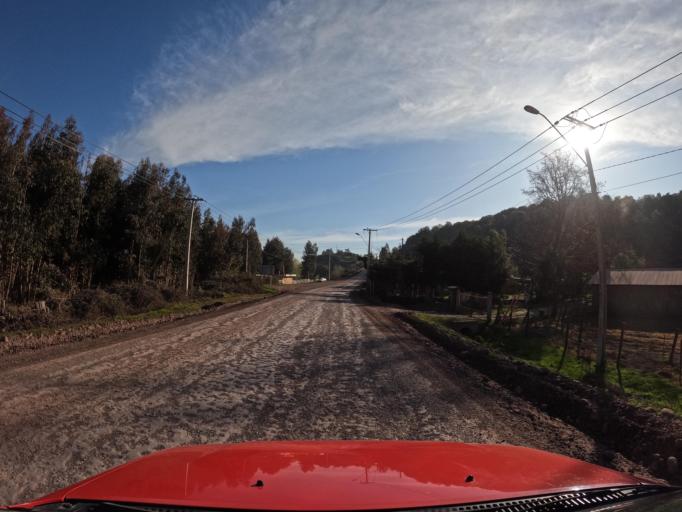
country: CL
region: Maule
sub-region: Provincia de Curico
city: Teno
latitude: -34.9688
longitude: -70.9450
